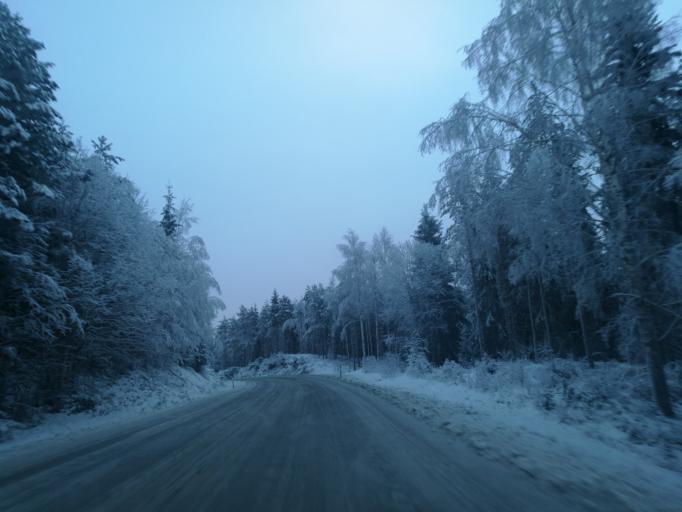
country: NO
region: Hedmark
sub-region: Kongsvinger
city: Kongsvinger
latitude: 60.2878
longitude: 12.1864
